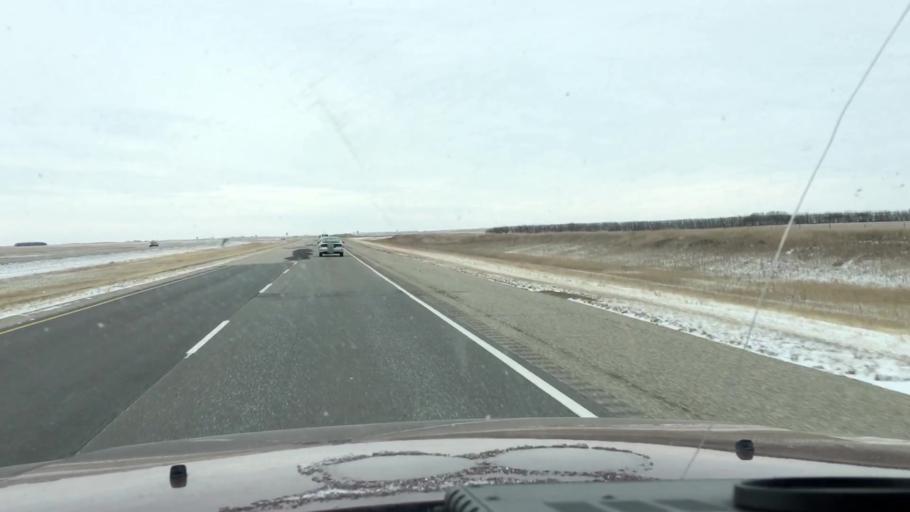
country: CA
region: Saskatchewan
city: Saskatoon
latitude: 51.4664
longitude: -106.2417
